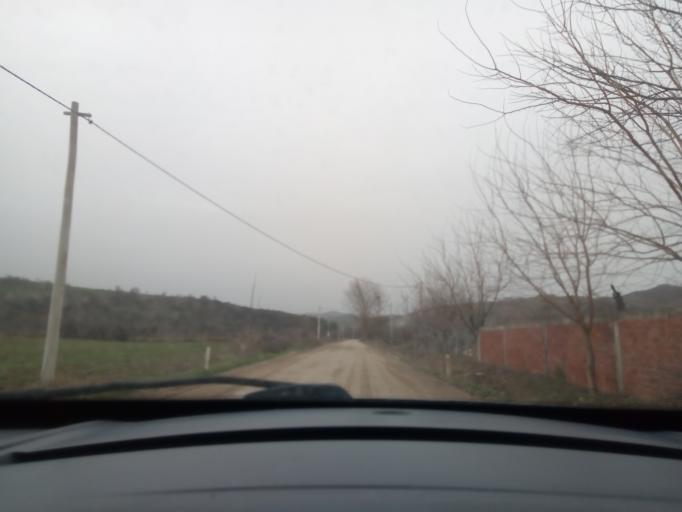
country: TR
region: Balikesir
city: Susurluk
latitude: 39.9209
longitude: 28.1382
